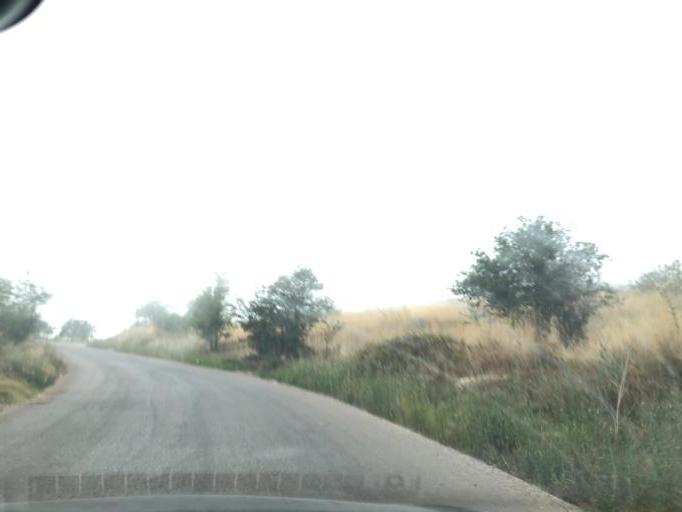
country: LB
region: Liban-Nord
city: Bcharre
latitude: 34.1279
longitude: 35.8830
